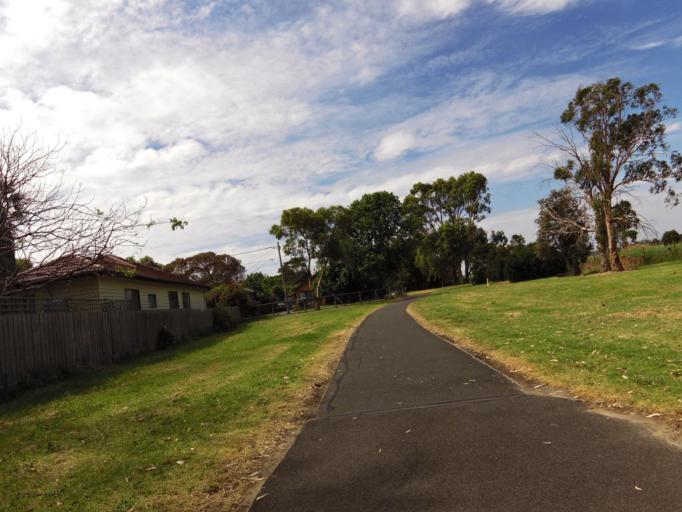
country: AU
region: Victoria
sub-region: Frankston
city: Seaford
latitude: -38.0999
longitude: 145.1343
